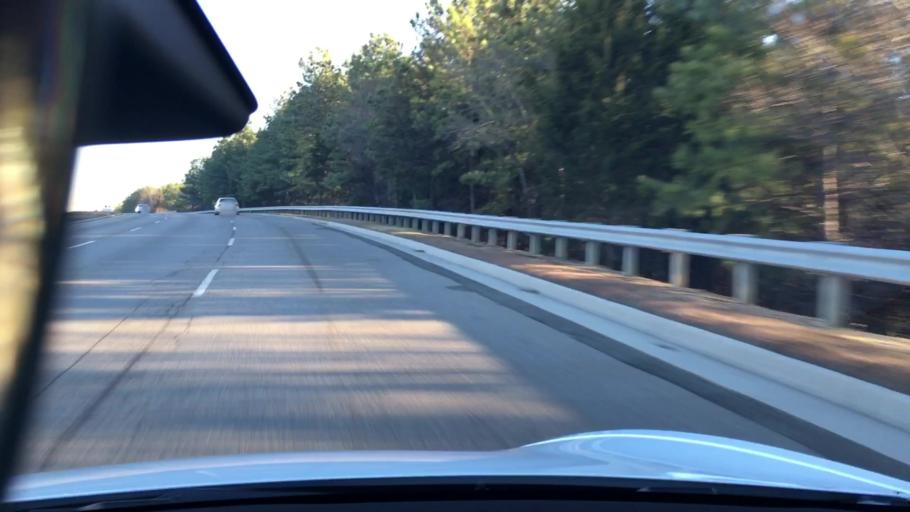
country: US
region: Virginia
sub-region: Henrico County
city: Fort Lee
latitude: 37.4966
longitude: -77.3506
